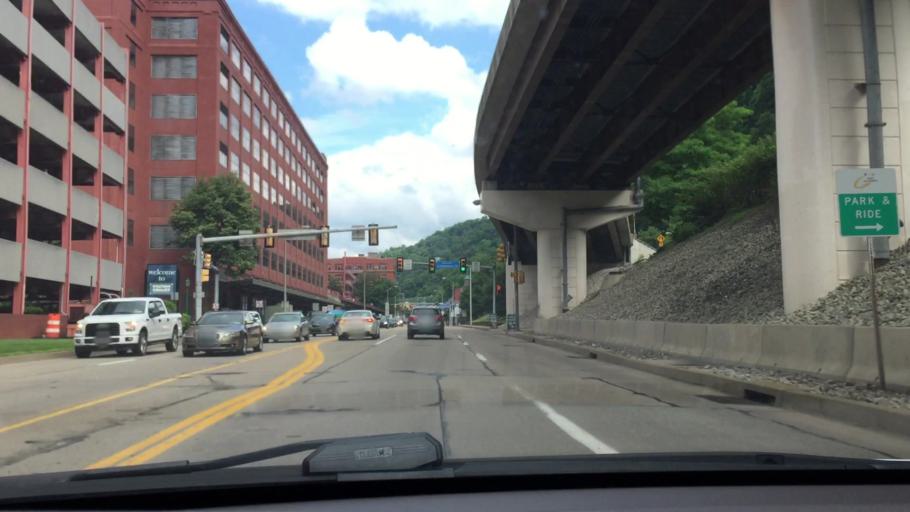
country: US
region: Pennsylvania
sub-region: Allegheny County
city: Pittsburgh
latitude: 40.4341
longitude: -80.0073
